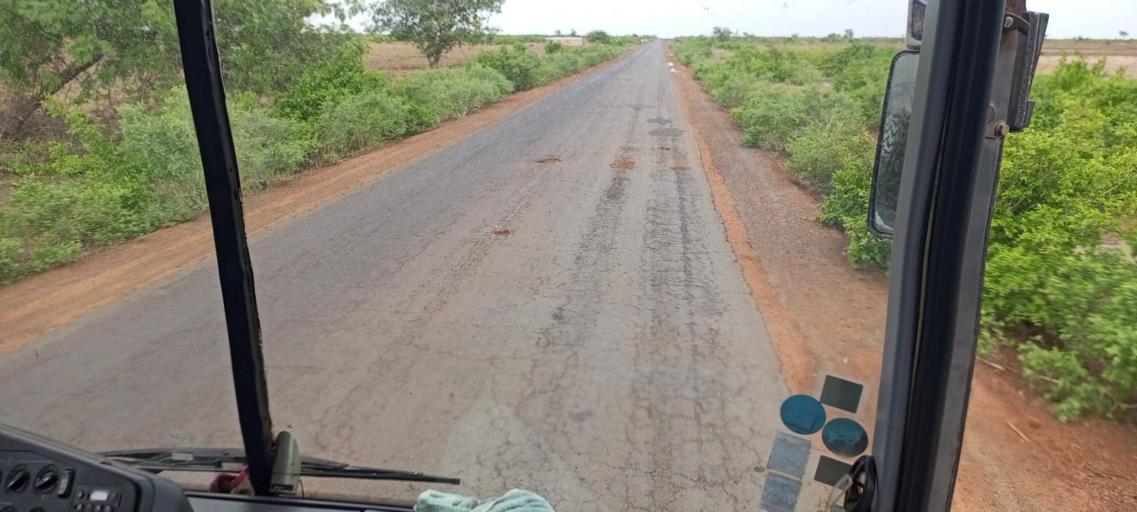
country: ML
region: Segou
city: Bla
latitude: 12.7089
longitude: -5.7244
